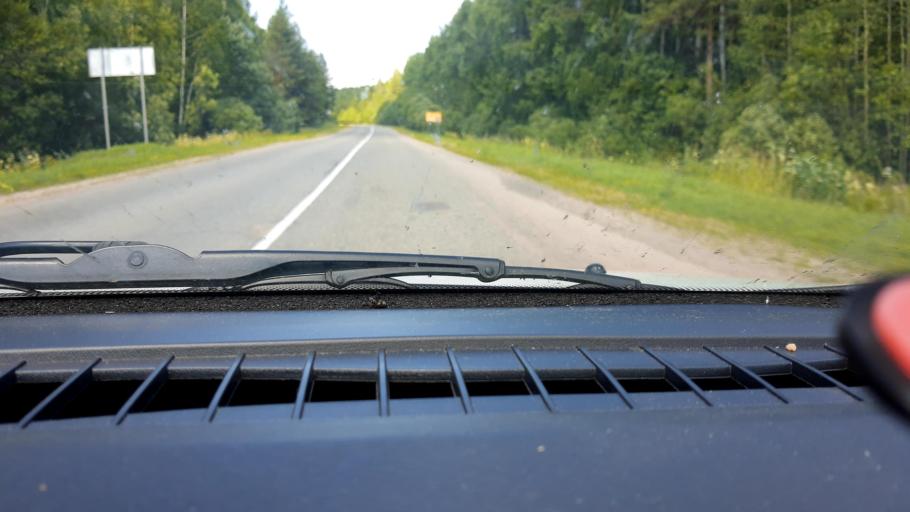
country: RU
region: Nizjnij Novgorod
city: Tonkino
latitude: 57.3245
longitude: 46.4753
